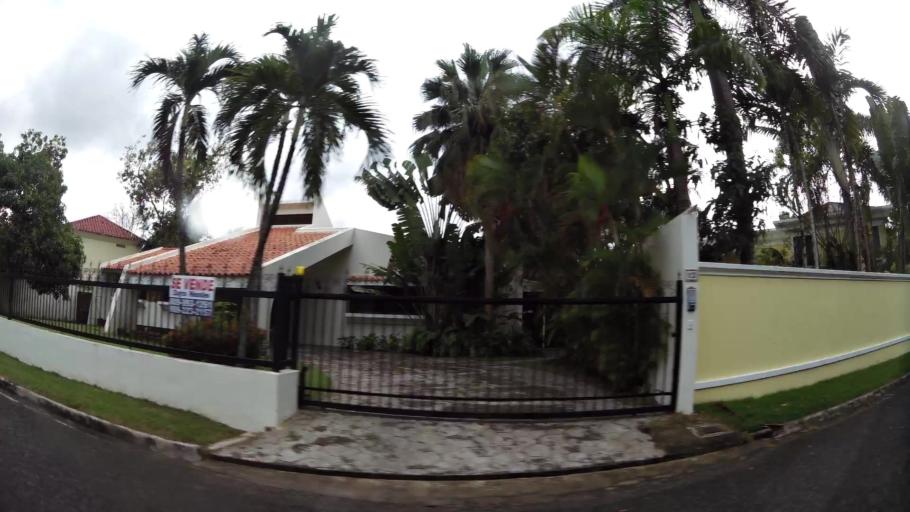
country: DO
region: Nacional
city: La Agustina
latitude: 18.5110
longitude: -69.9490
